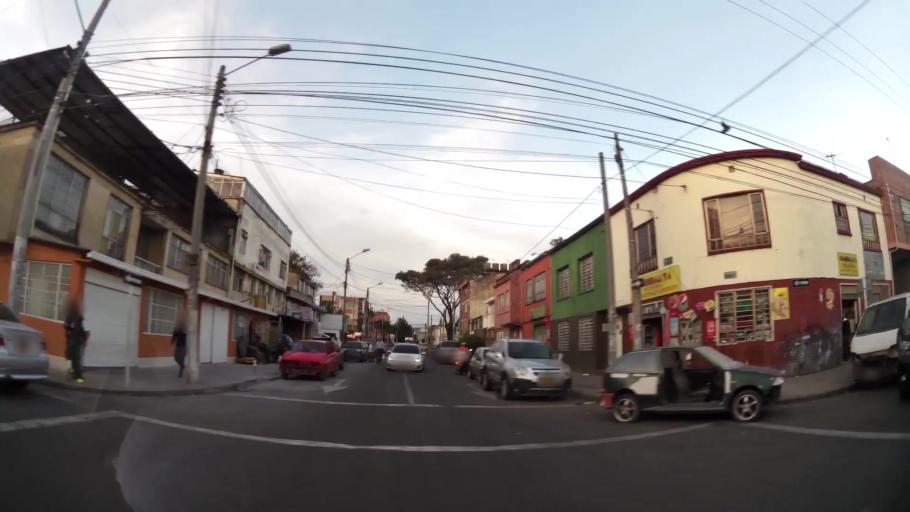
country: CO
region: Bogota D.C.
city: Barrio San Luis
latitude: 4.6614
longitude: -74.0662
